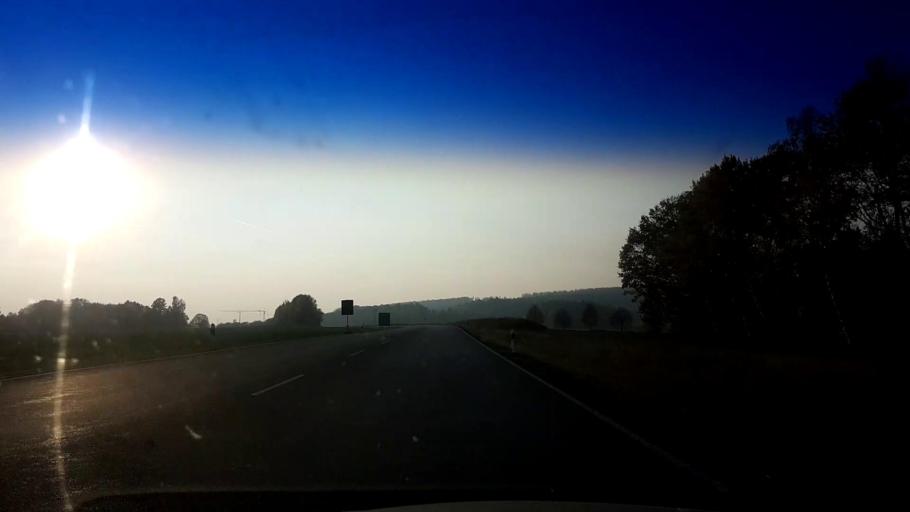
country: DE
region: Bavaria
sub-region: Upper Franconia
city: Hohenberg an der Eger
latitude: 50.0850
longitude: 12.2145
